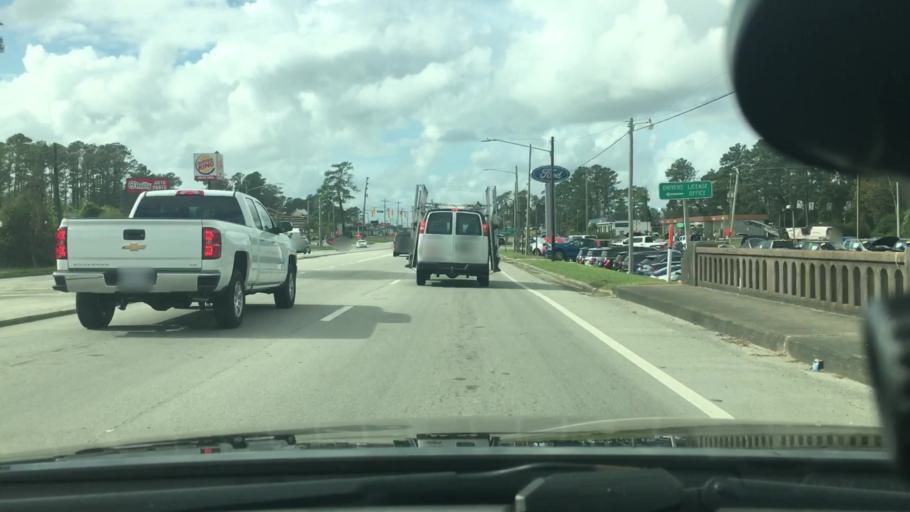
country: US
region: North Carolina
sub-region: Craven County
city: Havelock
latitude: 34.8819
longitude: -76.9085
